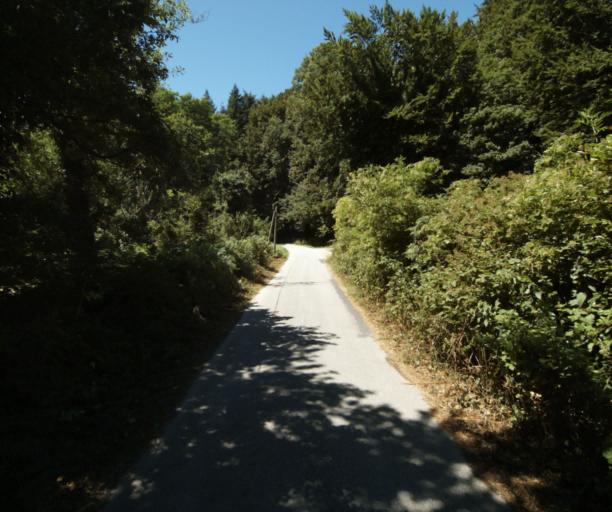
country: FR
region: Languedoc-Roussillon
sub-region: Departement de l'Aude
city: Cuxac-Cabardes
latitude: 43.4014
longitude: 2.2241
